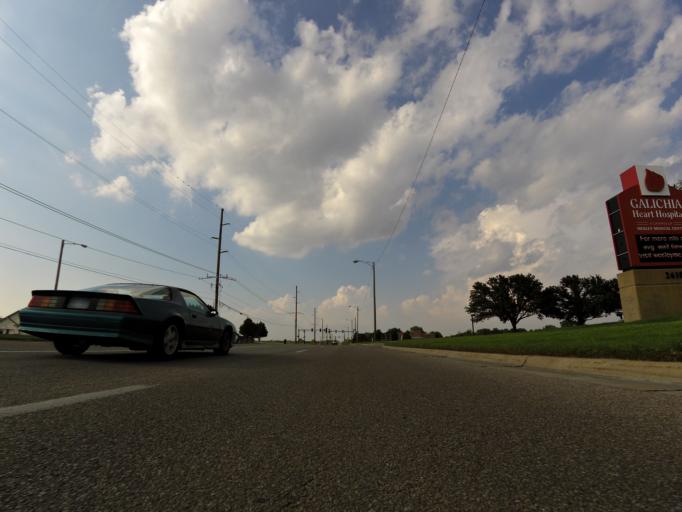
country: US
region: Kansas
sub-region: Sedgwick County
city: Bellaire
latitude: 37.7315
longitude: -97.2624
